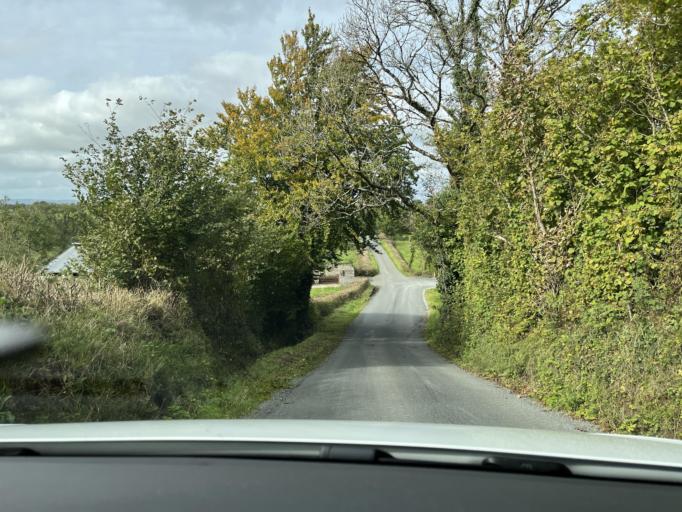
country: IE
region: Connaught
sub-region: County Leitrim
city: Carrick-on-Shannon
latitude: 53.9574
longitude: -8.0675
